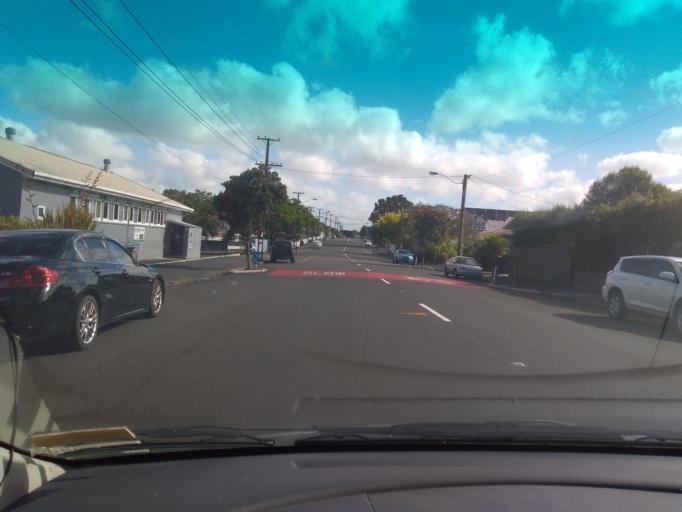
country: NZ
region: Auckland
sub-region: Auckland
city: Rosebank
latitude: -36.8562
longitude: 174.7036
